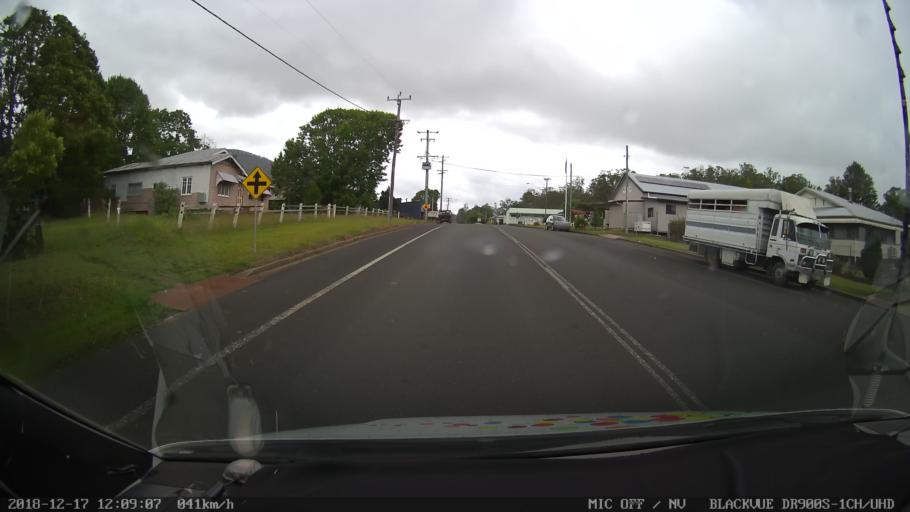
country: AU
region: New South Wales
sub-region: Kyogle
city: Kyogle
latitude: -28.4737
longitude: 152.5490
